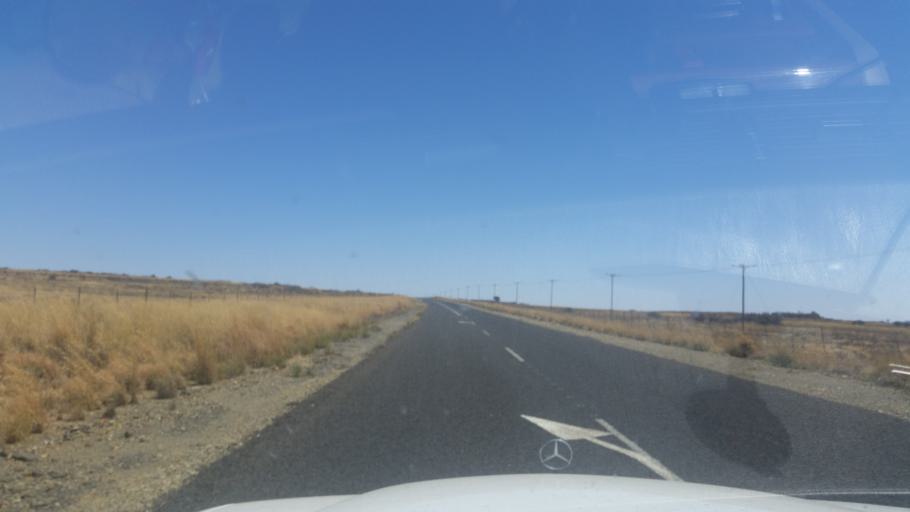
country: ZA
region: Northern Cape
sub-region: Pixley ka Seme District Municipality
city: Colesberg
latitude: -30.7009
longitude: 25.1839
